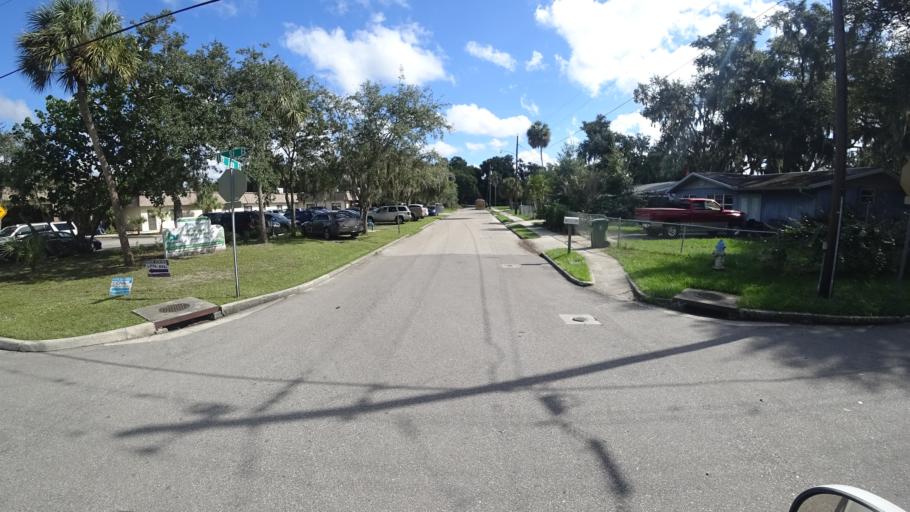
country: US
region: Florida
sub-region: Manatee County
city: Bradenton
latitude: 27.4982
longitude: -82.5480
